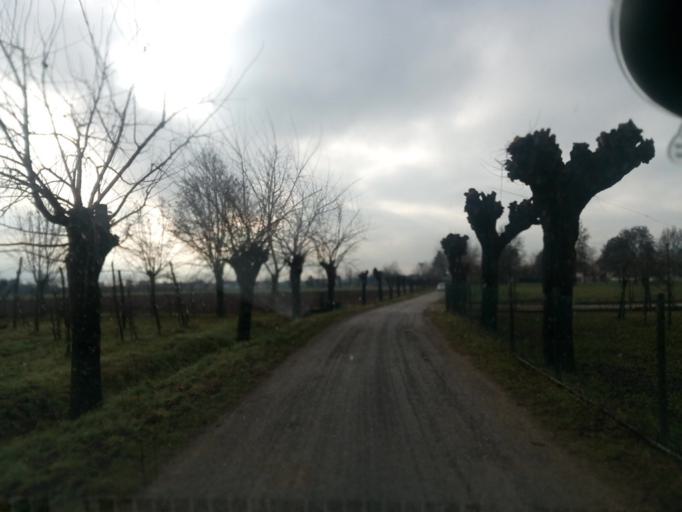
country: IT
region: Veneto
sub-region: Provincia di Vicenza
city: Sandrigo
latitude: 45.6740
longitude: 11.5841
